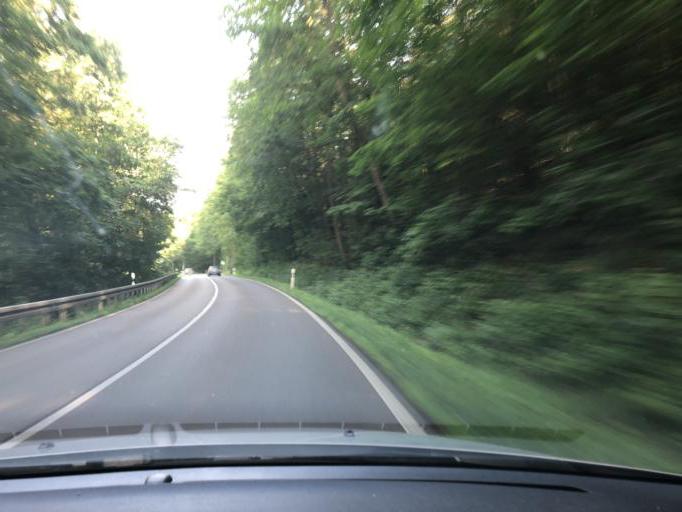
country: DE
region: Saxony
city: Bannewitz
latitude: 50.9854
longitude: 13.6956
